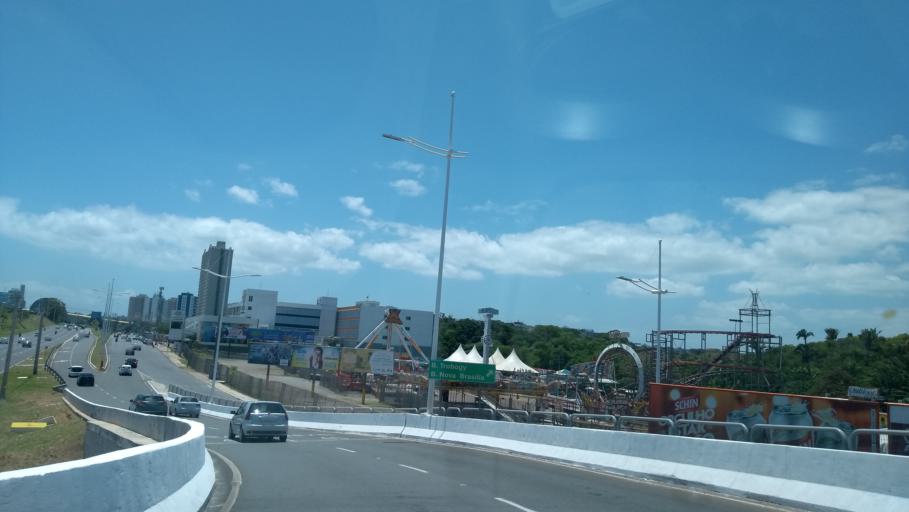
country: BR
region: Bahia
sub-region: Lauro De Freitas
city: Lauro de Freitas
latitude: -12.9364
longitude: -38.3987
